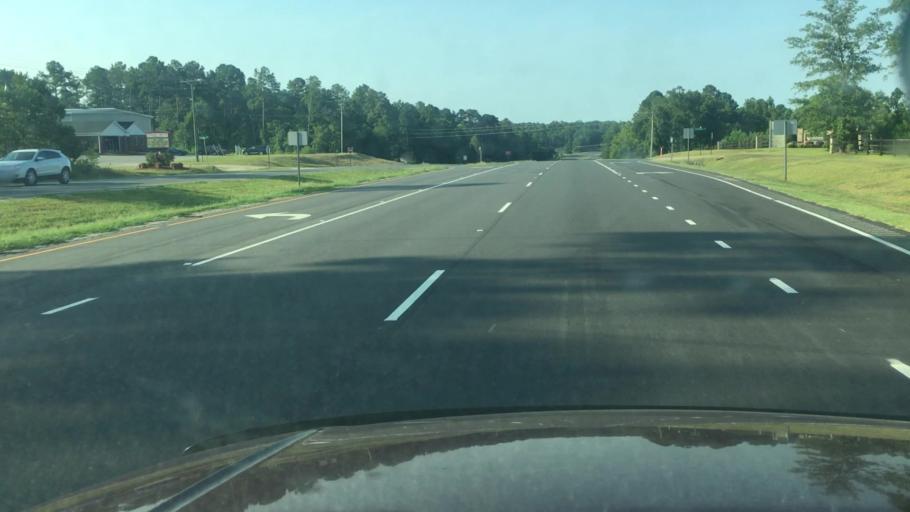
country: US
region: North Carolina
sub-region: Robeson County
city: Saint Pauls
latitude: 34.8648
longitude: -78.8501
